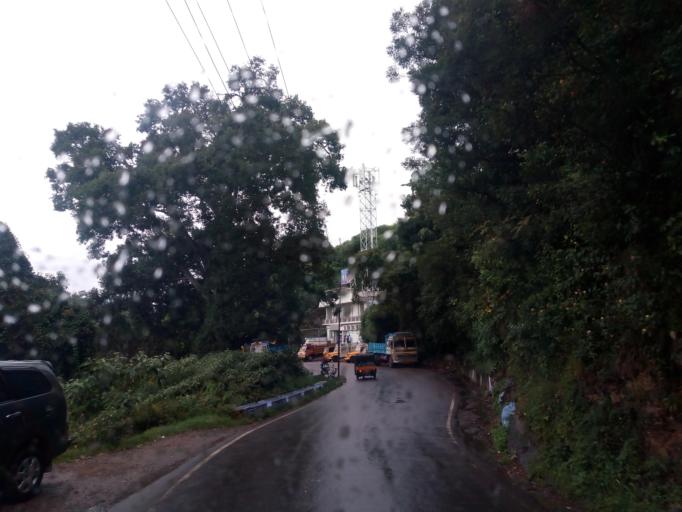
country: IN
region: Tamil Nadu
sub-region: Nilgiri
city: Wellington
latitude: 11.3432
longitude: 76.7974
